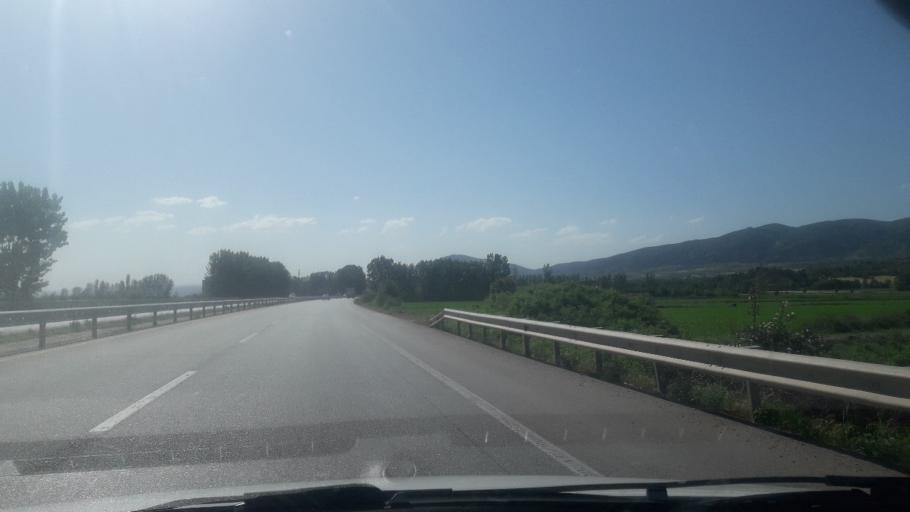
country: TR
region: Tokat
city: Dokmetepe
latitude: 40.3049
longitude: 36.3100
